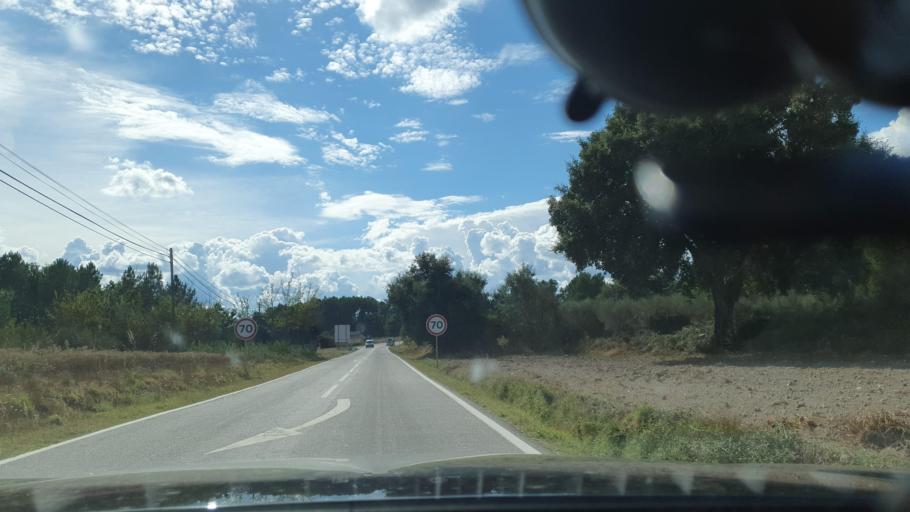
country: PT
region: Vila Real
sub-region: Chaves
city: Chaves
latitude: 41.7106
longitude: -7.5512
